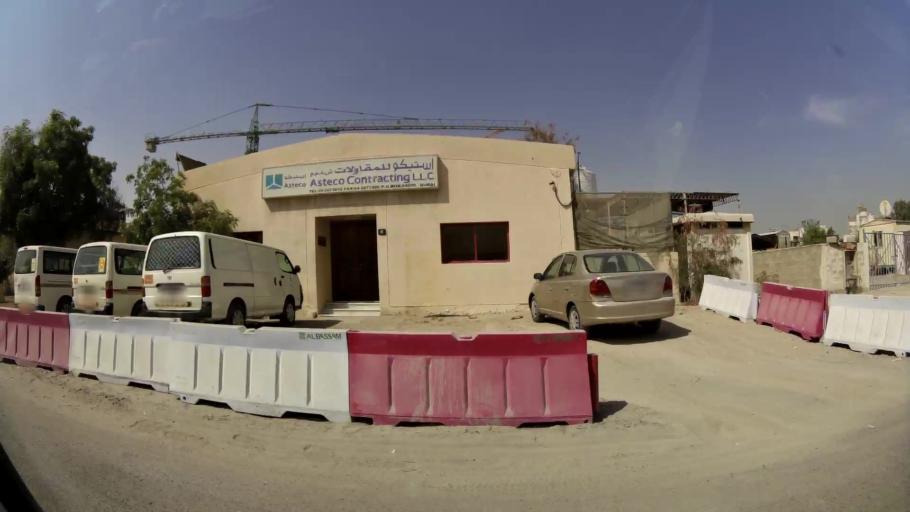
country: AE
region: Ash Shariqah
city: Sharjah
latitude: 25.2796
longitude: 55.3900
